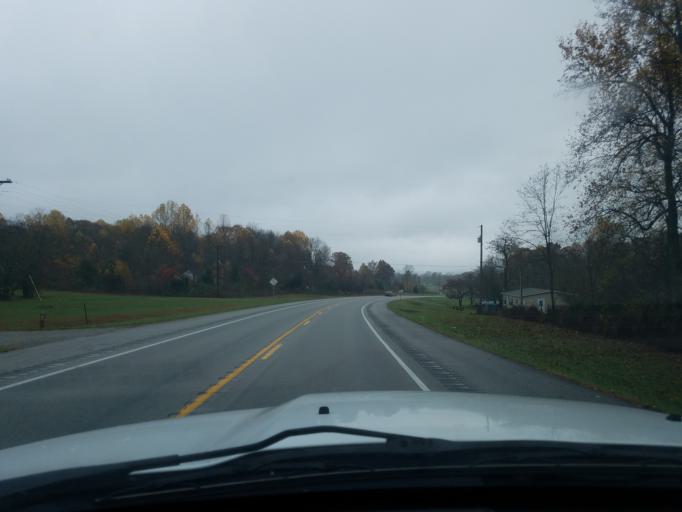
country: US
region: Kentucky
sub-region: Taylor County
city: Campbellsville
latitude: 37.3850
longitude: -85.4173
